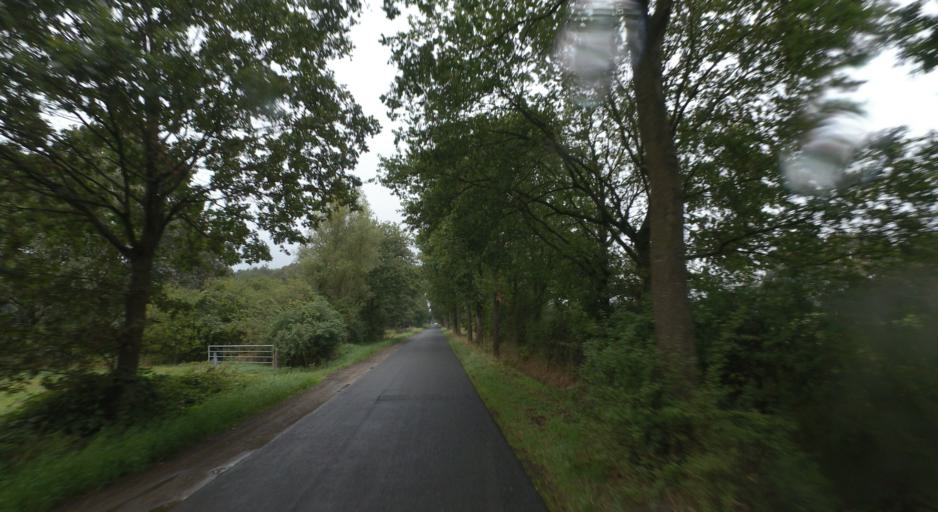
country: DE
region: North Rhine-Westphalia
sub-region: Regierungsbezirk Dusseldorf
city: Hamminkeln
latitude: 51.7169
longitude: 6.6121
